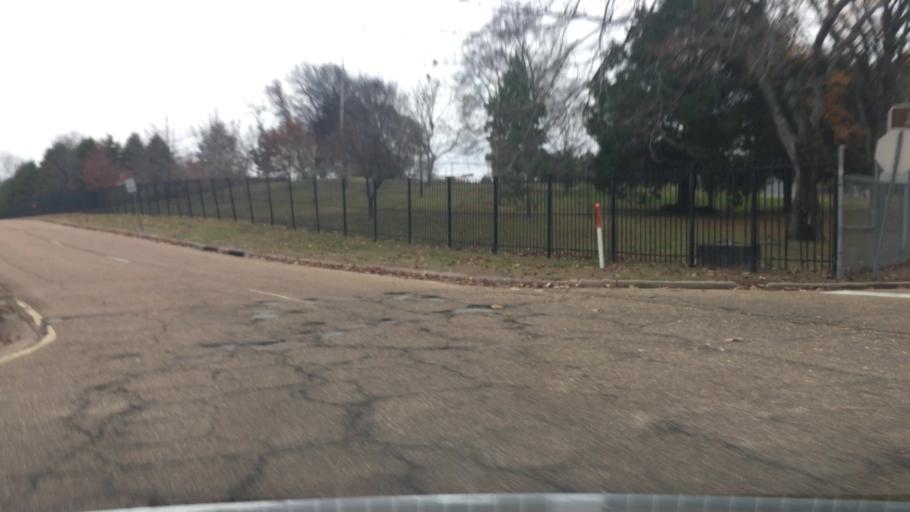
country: US
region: Mississippi
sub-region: Rankin County
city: Flowood
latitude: 32.3237
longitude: -90.1584
